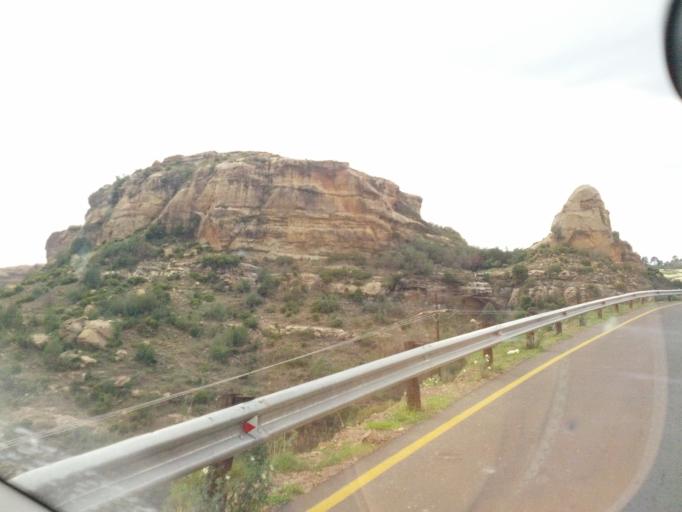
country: LS
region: Maseru
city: Nako
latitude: -29.4804
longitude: 27.7404
